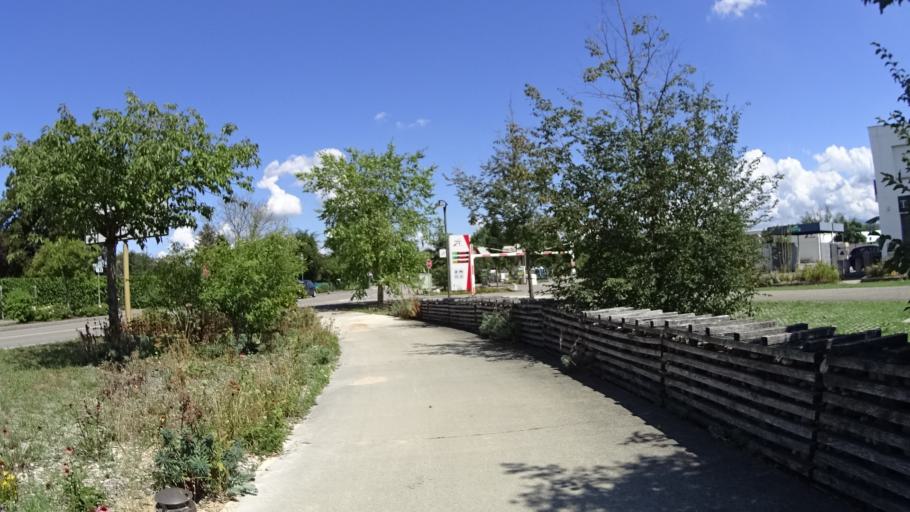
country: FR
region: Alsace
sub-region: Departement du Haut-Rhin
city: Chalampe
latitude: 47.8164
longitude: 7.5399
